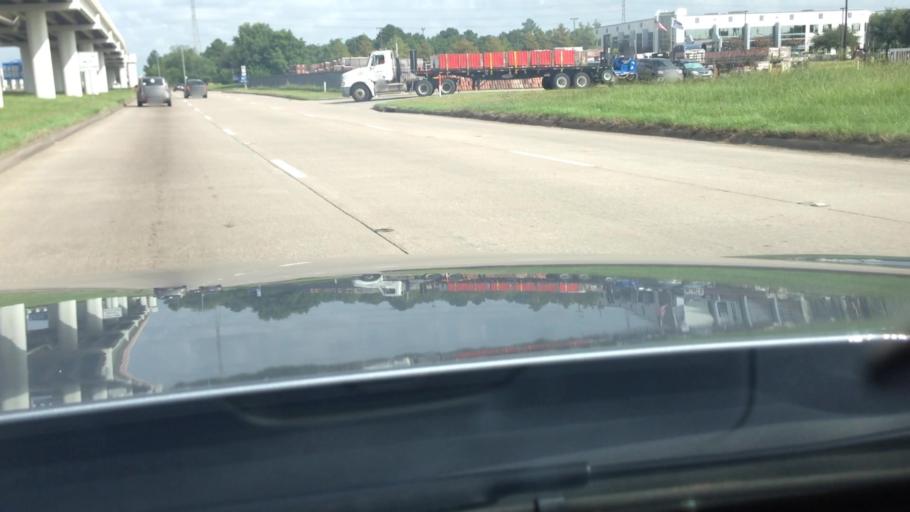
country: US
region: Texas
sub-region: Harris County
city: Hudson
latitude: 29.9390
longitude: -95.5182
